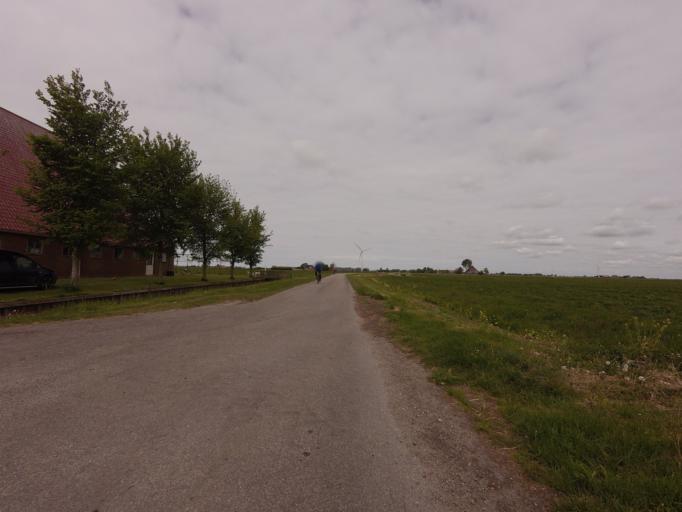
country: NL
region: Friesland
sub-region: Sudwest Fryslan
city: Workum
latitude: 52.9543
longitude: 5.4708
